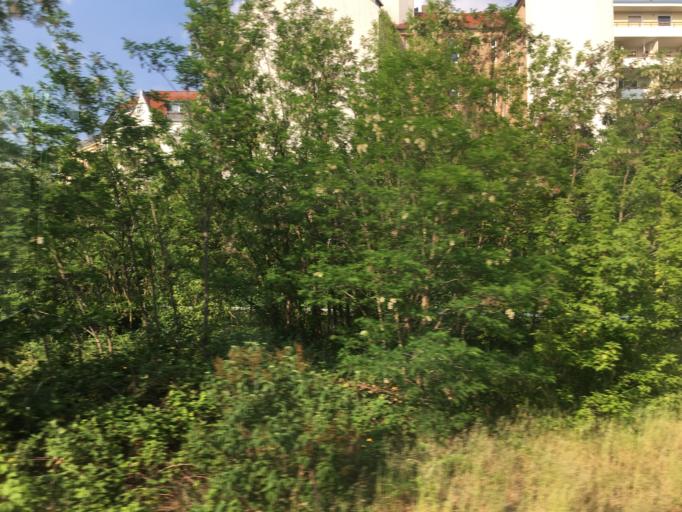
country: DE
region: Berlin
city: Halensee
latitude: 52.4982
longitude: 13.2877
